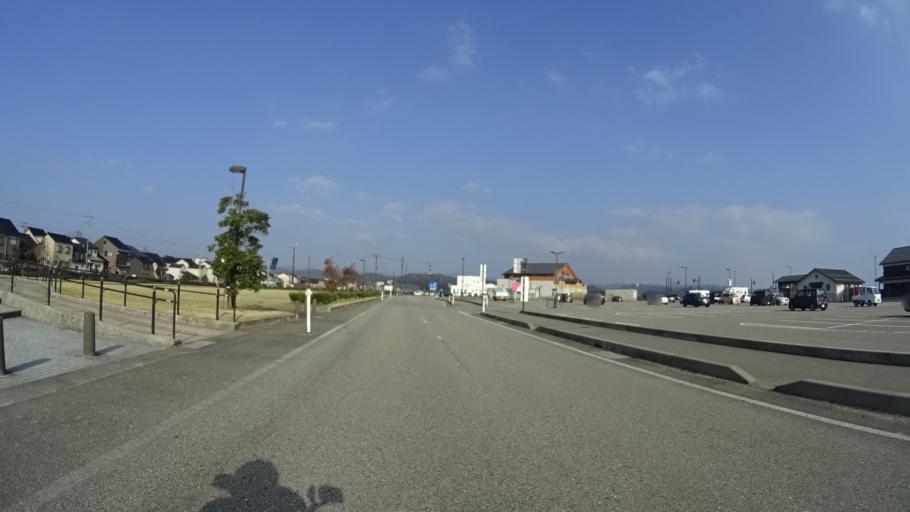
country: JP
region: Toyama
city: Himi
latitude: 36.8644
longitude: 136.9863
